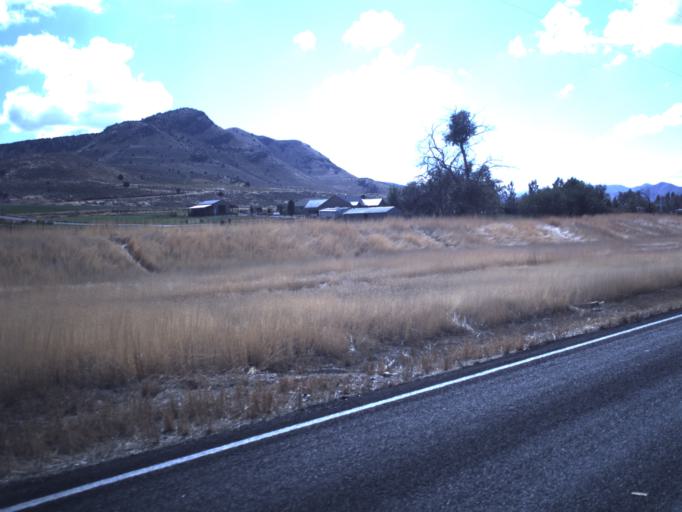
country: US
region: Utah
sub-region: Utah County
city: Genola
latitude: 39.9798
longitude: -111.8443
